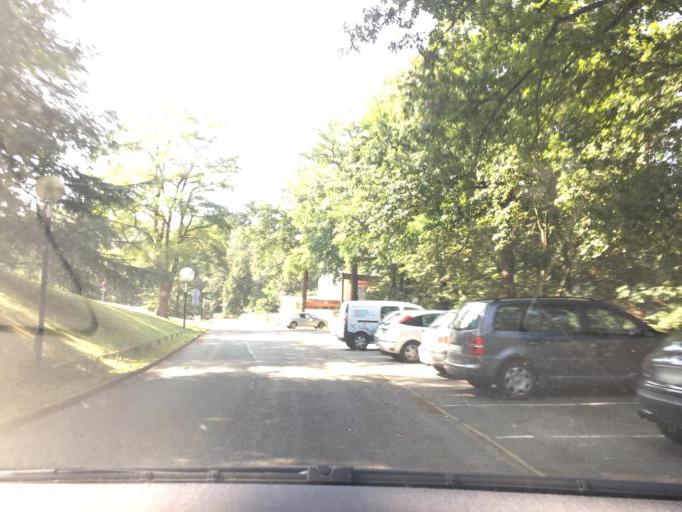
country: FR
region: Ile-de-France
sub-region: Departement des Yvelines
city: Jouy-en-Josas
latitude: 48.7600
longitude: 2.1709
